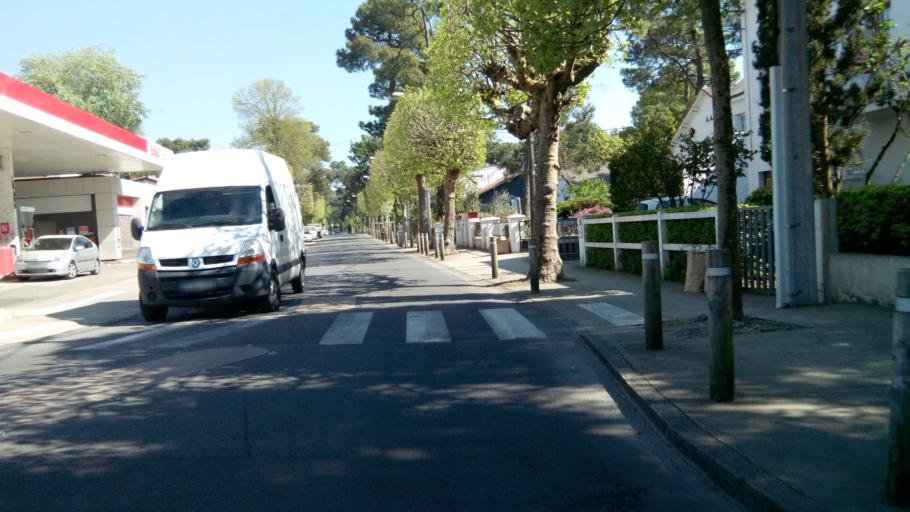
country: FR
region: Pays de la Loire
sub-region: Departement de la Loire-Atlantique
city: La Baule-Escoublac
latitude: 47.2873
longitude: -2.3807
